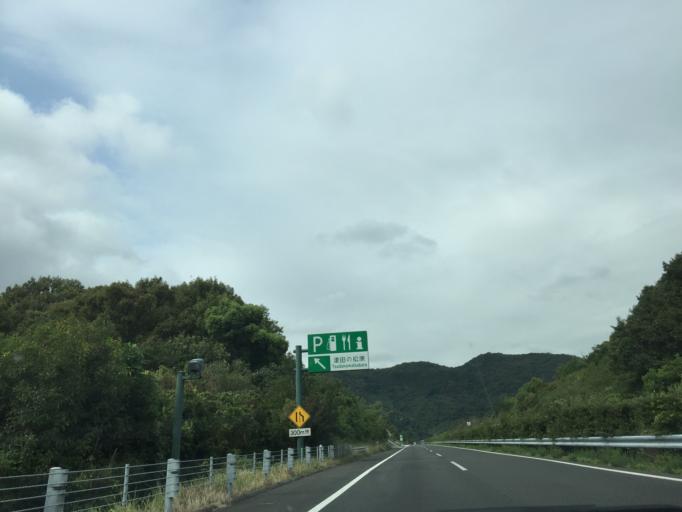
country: JP
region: Kagawa
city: Shido
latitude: 34.2761
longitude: 134.2699
